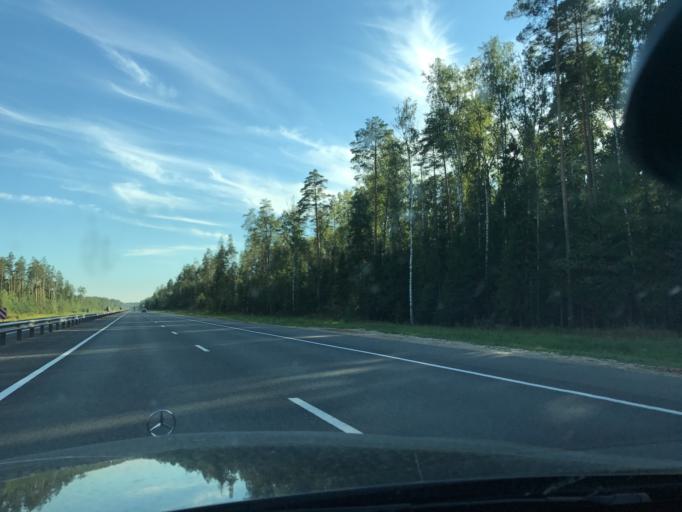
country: RU
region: Vladimir
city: Kameshkovo
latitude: 56.1702
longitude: 40.9391
